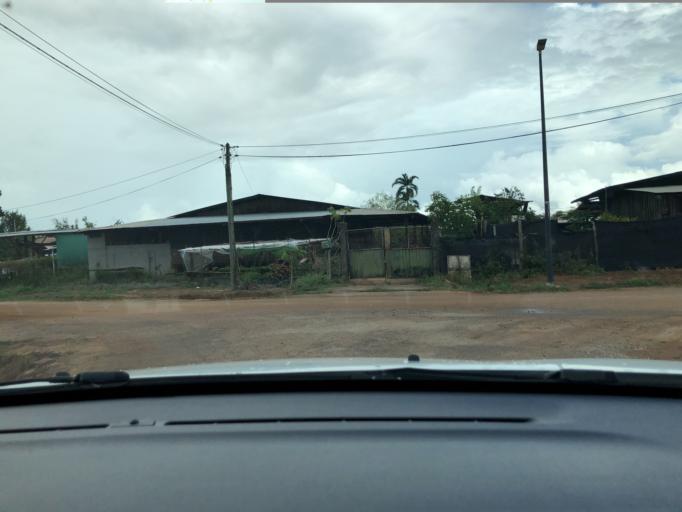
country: GF
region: Guyane
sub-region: Guyane
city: Mana
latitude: 5.6082
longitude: -53.8200
